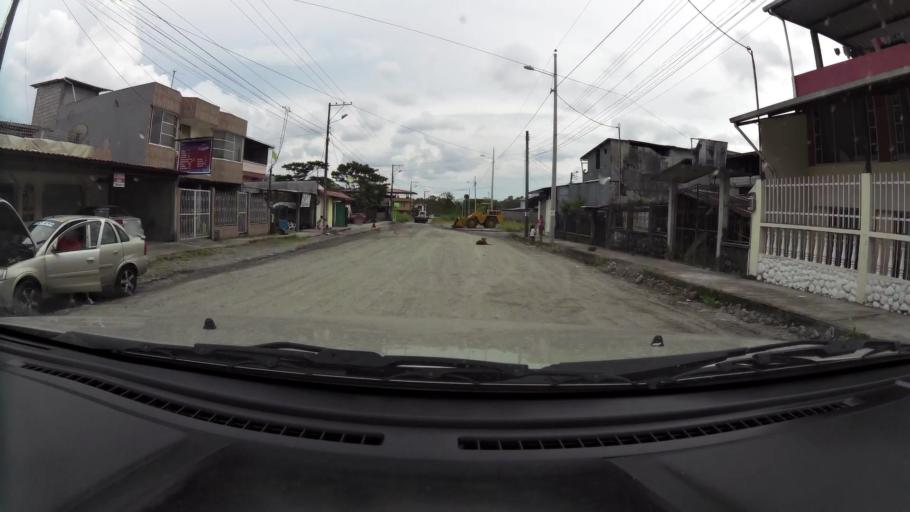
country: EC
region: Pastaza
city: Puyo
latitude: -1.4926
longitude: -78.0058
